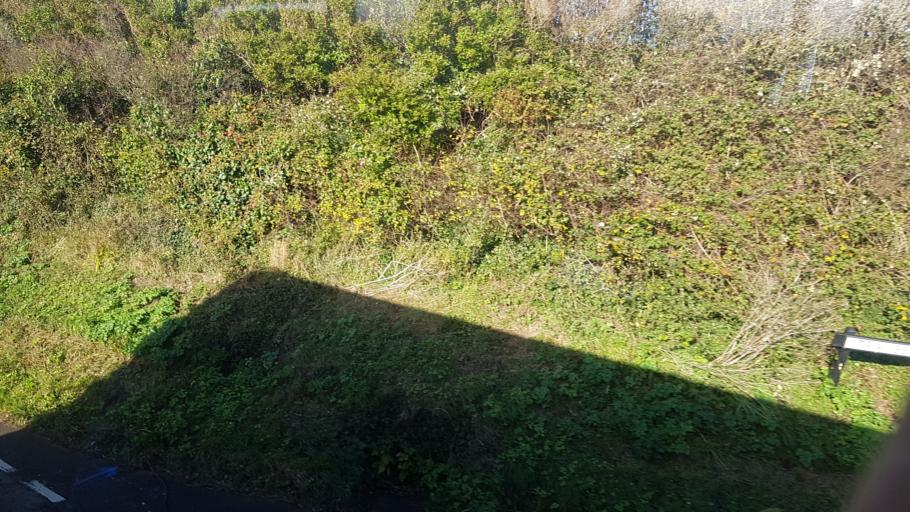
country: GB
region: England
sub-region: Isle of Wight
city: Shalfleet
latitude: 50.6502
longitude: -1.4197
